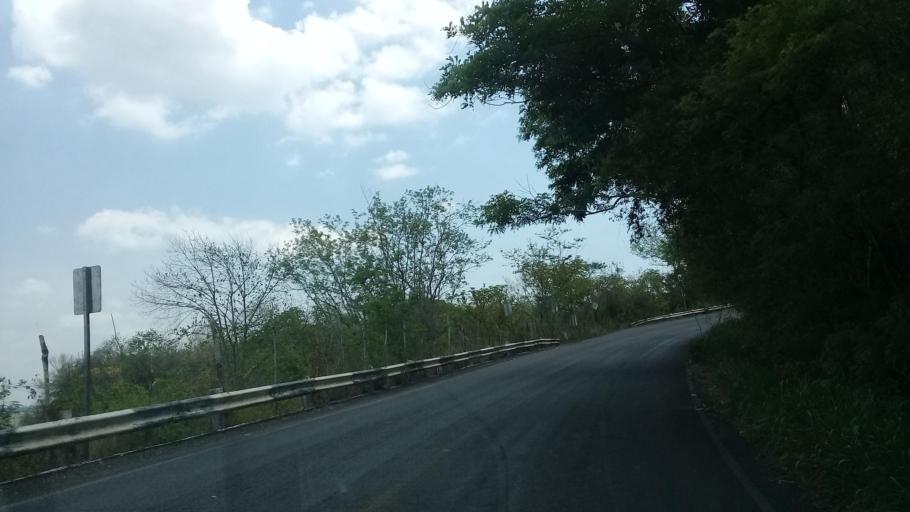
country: MX
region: Veracruz
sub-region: Emiliano Zapata
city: Plan del Rio
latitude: 19.4163
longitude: -96.6125
